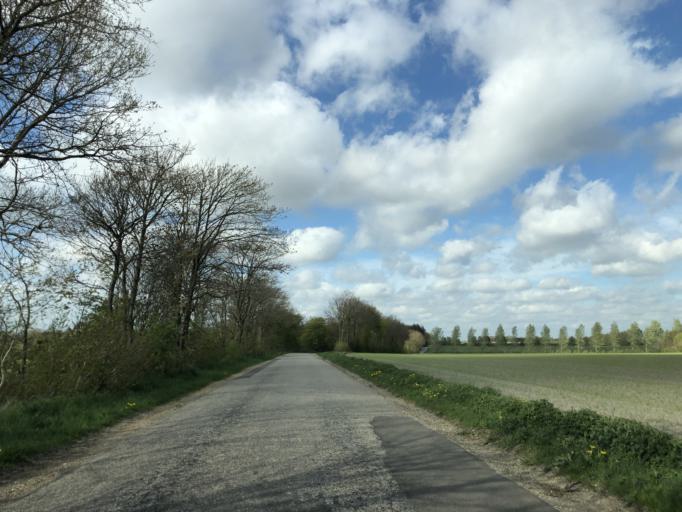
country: DK
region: Central Jutland
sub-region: Herning Kommune
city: Avlum
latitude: 56.2929
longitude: 8.6989
